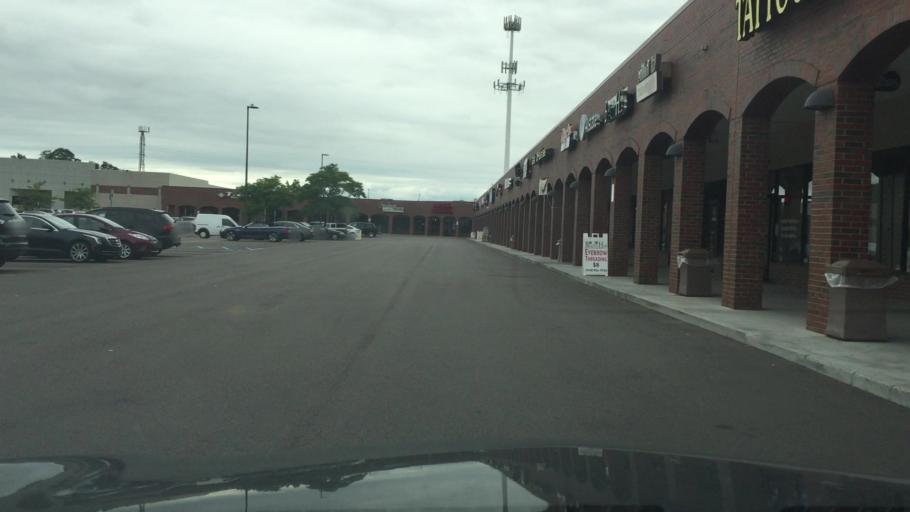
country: US
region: Michigan
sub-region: Oakland County
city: Walled Lake
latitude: 42.5285
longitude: -83.4385
